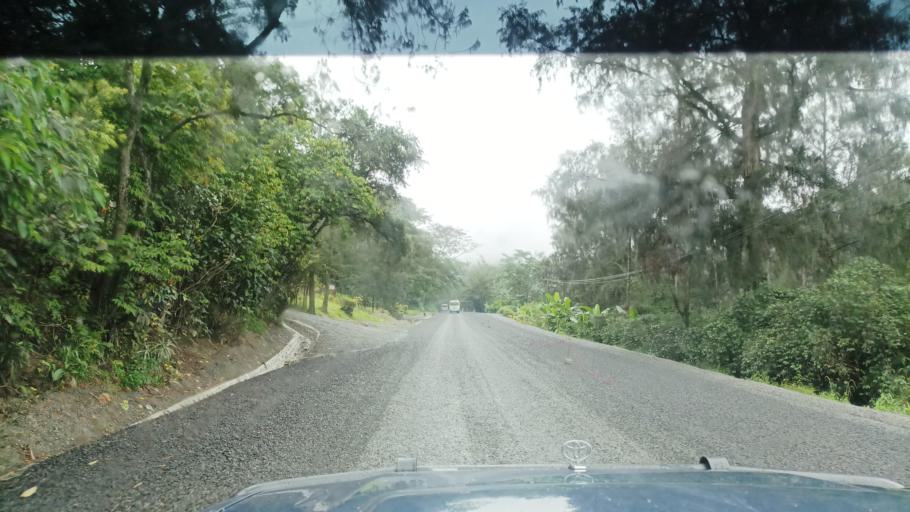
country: PG
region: Western Highlands
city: Rauna
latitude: -5.8325
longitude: 144.3621
